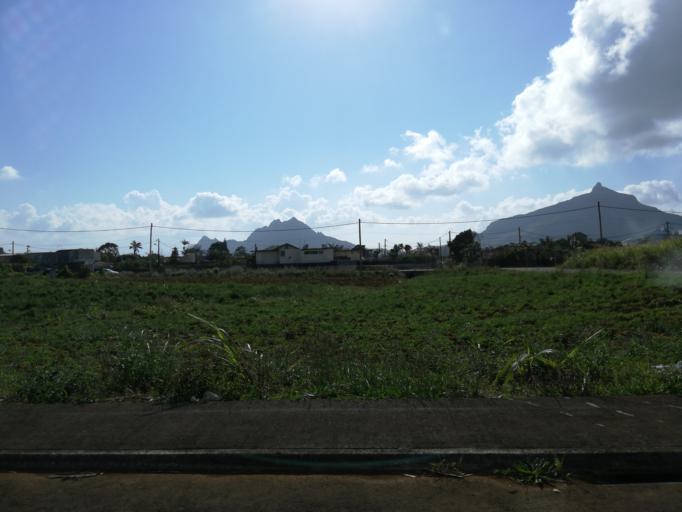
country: MU
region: Moka
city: Verdun
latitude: -20.2232
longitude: 57.5475
